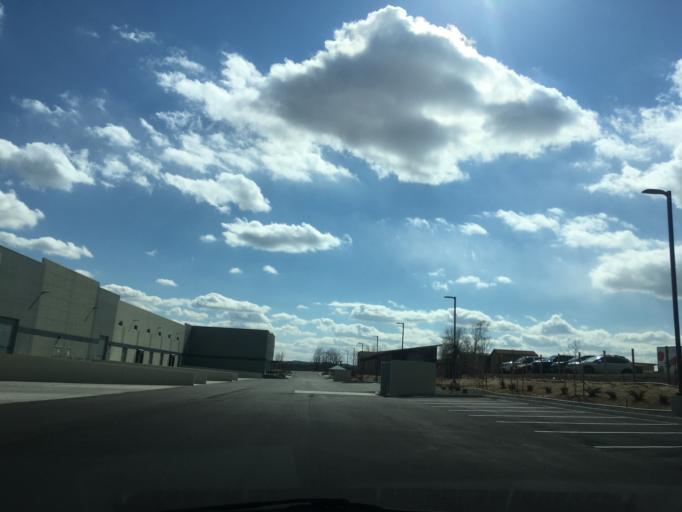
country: US
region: Colorado
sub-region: Boulder County
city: Louisville
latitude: 39.9599
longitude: -105.1184
